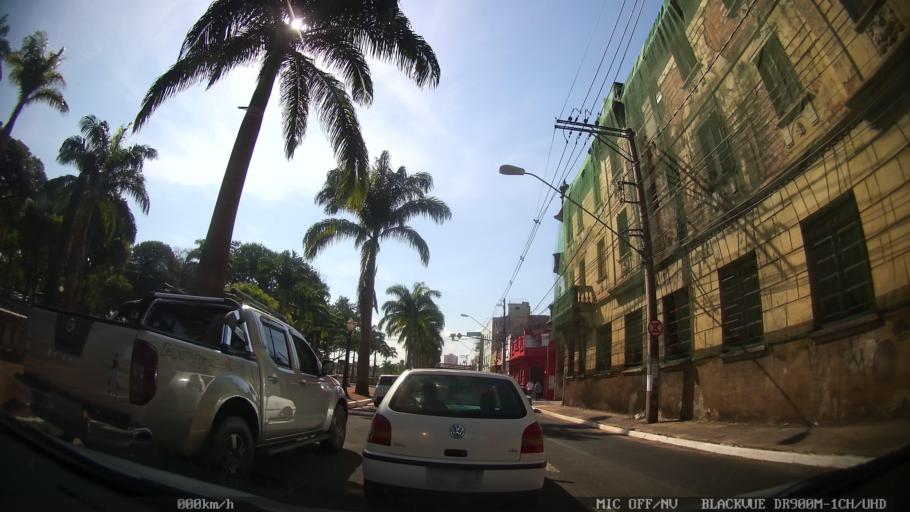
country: BR
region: Sao Paulo
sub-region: Ribeirao Preto
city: Ribeirao Preto
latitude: -21.1730
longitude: -47.8130
